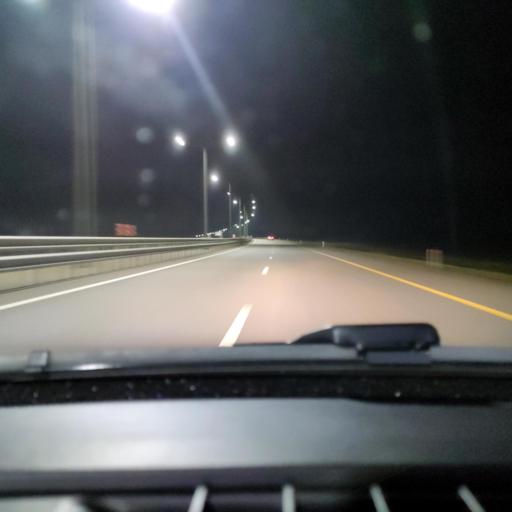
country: RU
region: Voronezj
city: Novaya Usman'
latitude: 51.5936
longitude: 39.3625
